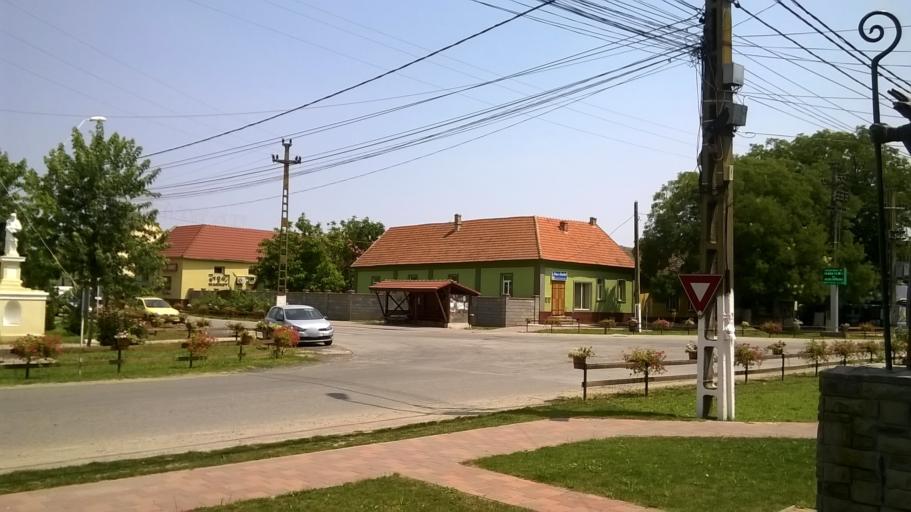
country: RO
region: Timis
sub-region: Comuna Dudestii Vechi
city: Dudestii Vechi
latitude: 46.0420
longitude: 20.4761
